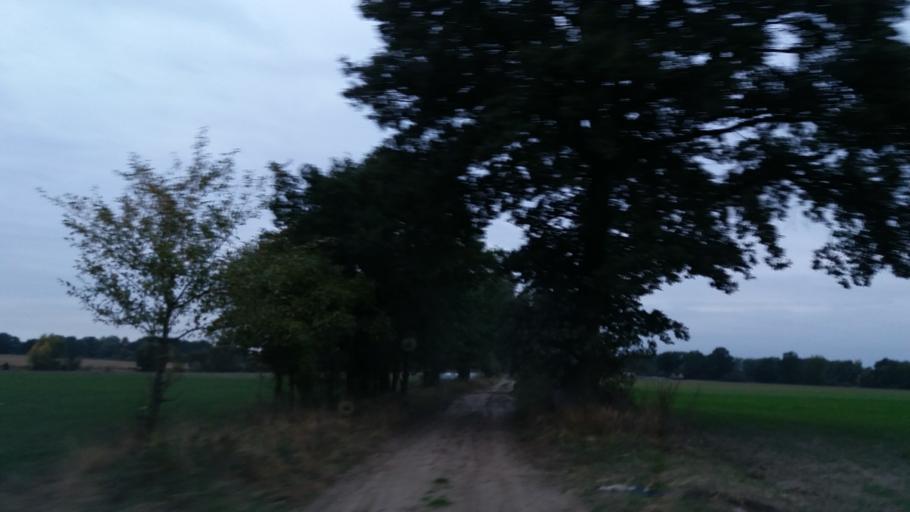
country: PL
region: West Pomeranian Voivodeship
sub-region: Powiat choszczenski
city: Choszczno
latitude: 53.0890
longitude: 15.4055
